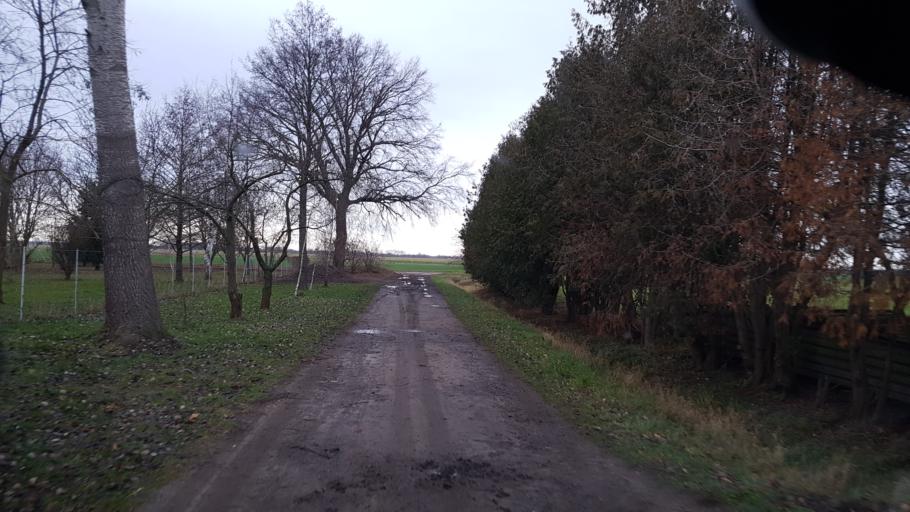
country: DE
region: Brandenburg
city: Doberlug-Kirchhain
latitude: 51.6519
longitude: 13.5483
